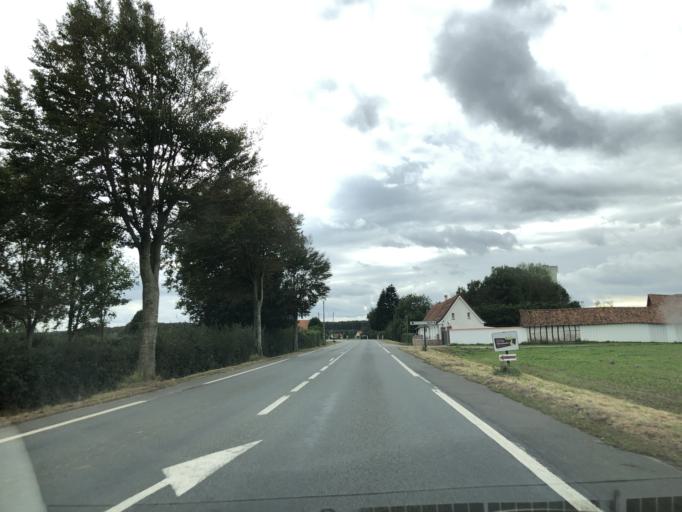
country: FR
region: Nord-Pas-de-Calais
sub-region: Departement du Pas-de-Calais
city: Hesdin
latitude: 50.4159
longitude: 2.0503
